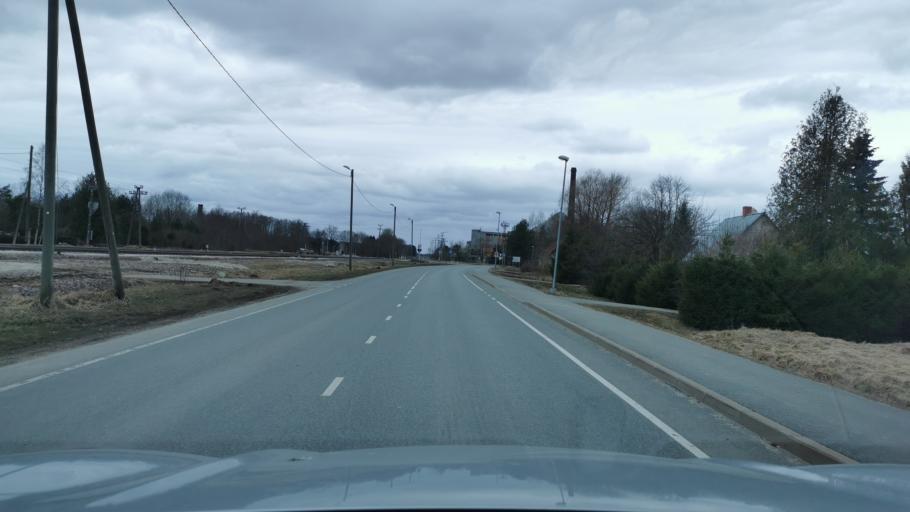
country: EE
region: Ida-Virumaa
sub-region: Puessi linn
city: Pussi
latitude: 59.3586
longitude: 27.0438
